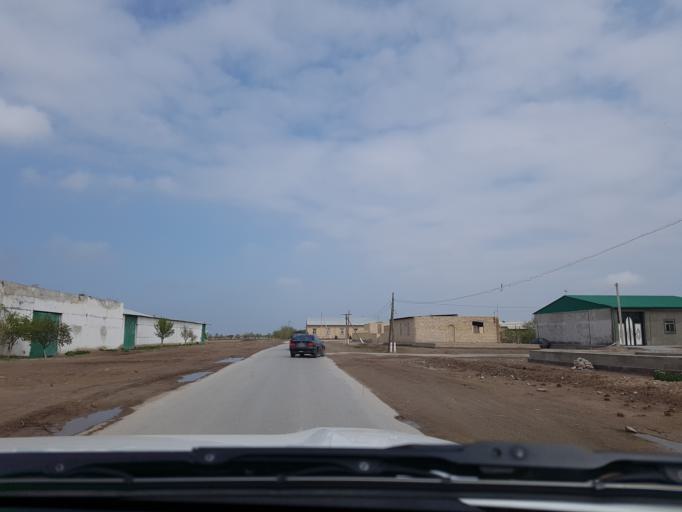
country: TM
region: Lebap
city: Turkmenabat
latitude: 38.9702
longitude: 63.6818
